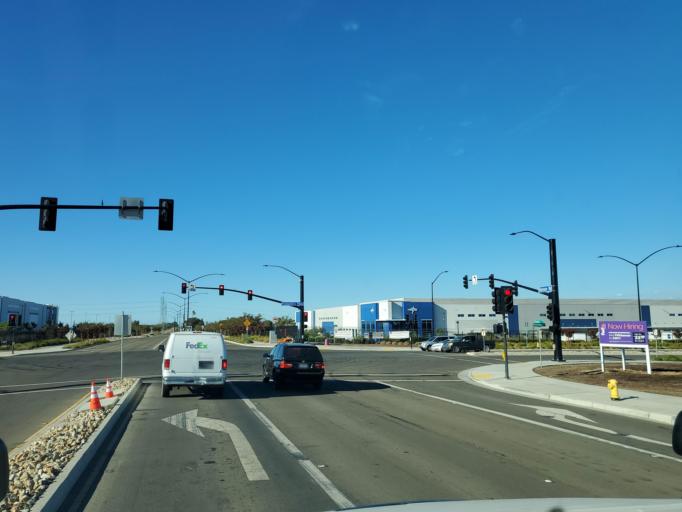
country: US
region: California
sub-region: San Joaquin County
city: Mountain House
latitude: 37.7325
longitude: -121.5132
